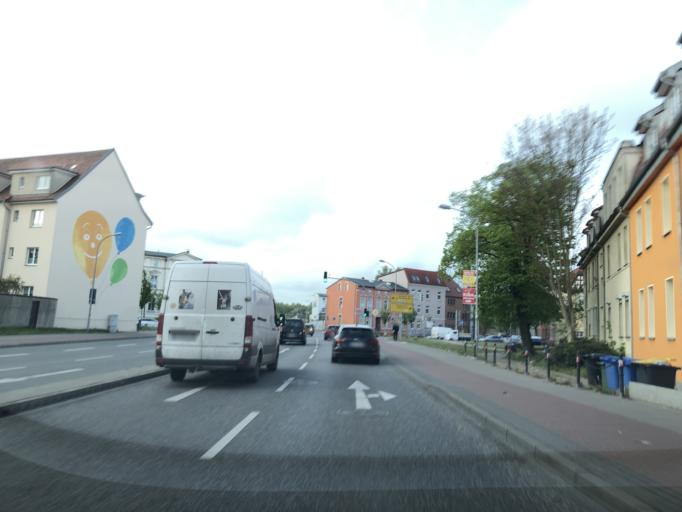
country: DE
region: Mecklenburg-Vorpommern
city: Guestrow
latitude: 53.8010
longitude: 12.1822
